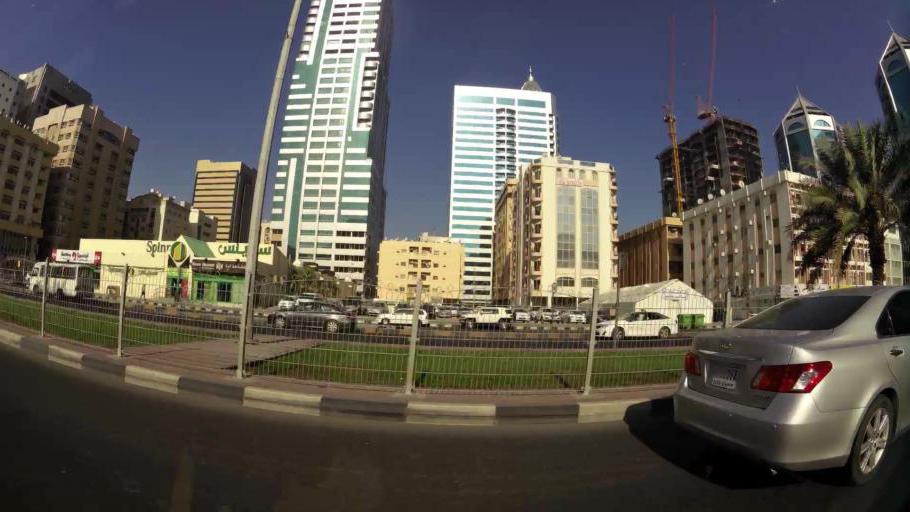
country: AE
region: Ash Shariqah
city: Sharjah
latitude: 25.3432
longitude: 55.3878
